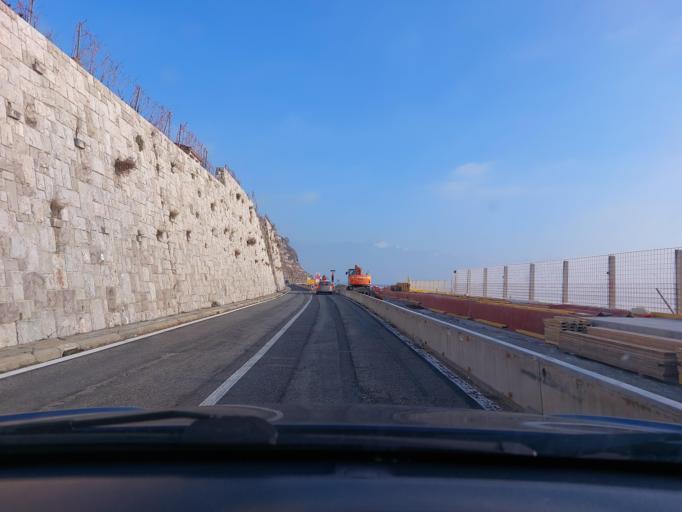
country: CH
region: Vaud
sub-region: Lavaux-Oron District
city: Chexbres
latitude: 46.4778
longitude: 6.7677
